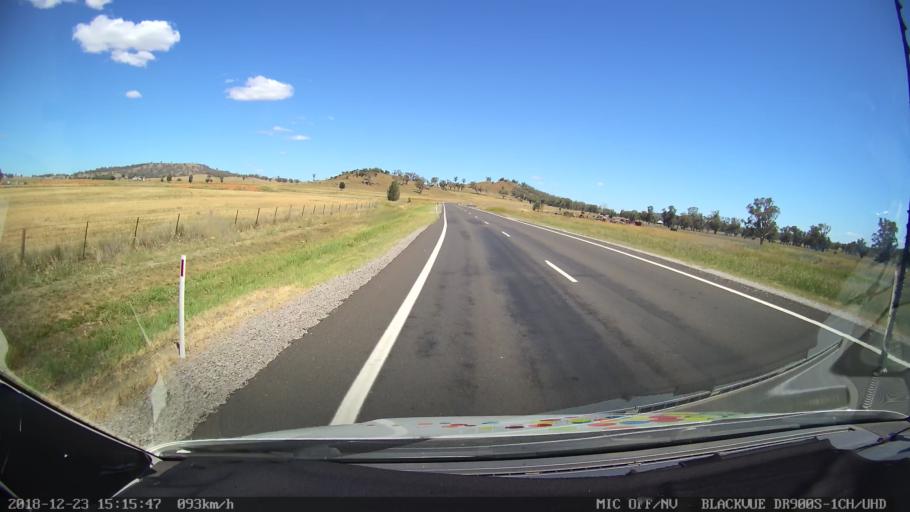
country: AU
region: New South Wales
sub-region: Tamworth Municipality
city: Manilla
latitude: -30.7909
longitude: 150.7447
